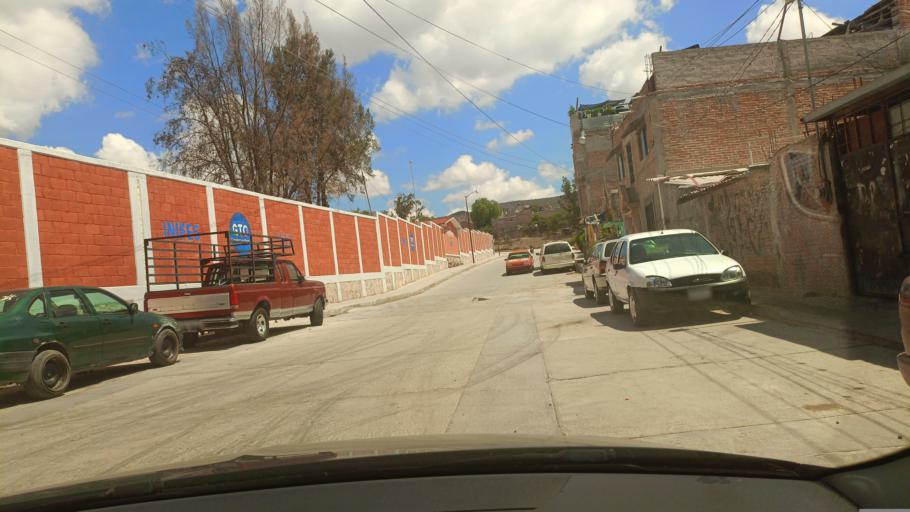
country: MX
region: Guanajuato
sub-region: San Luis de la Paz
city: San Luis de la Paz
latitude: 21.3022
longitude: -100.5049
